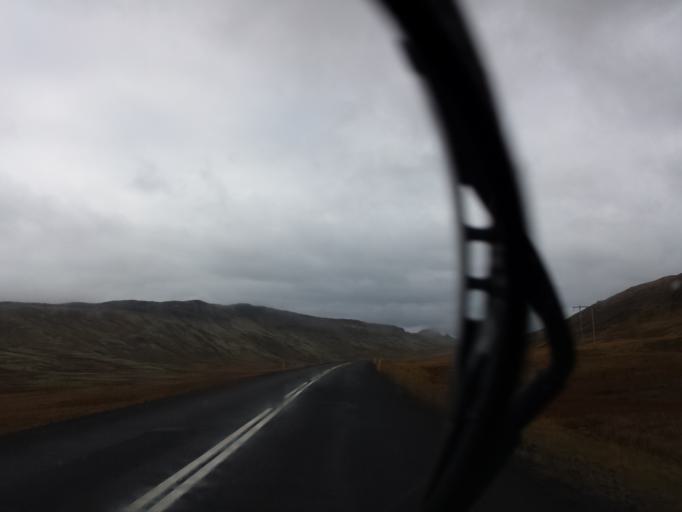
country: IS
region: West
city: Stykkisholmur
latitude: 64.8859
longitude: -22.8154
